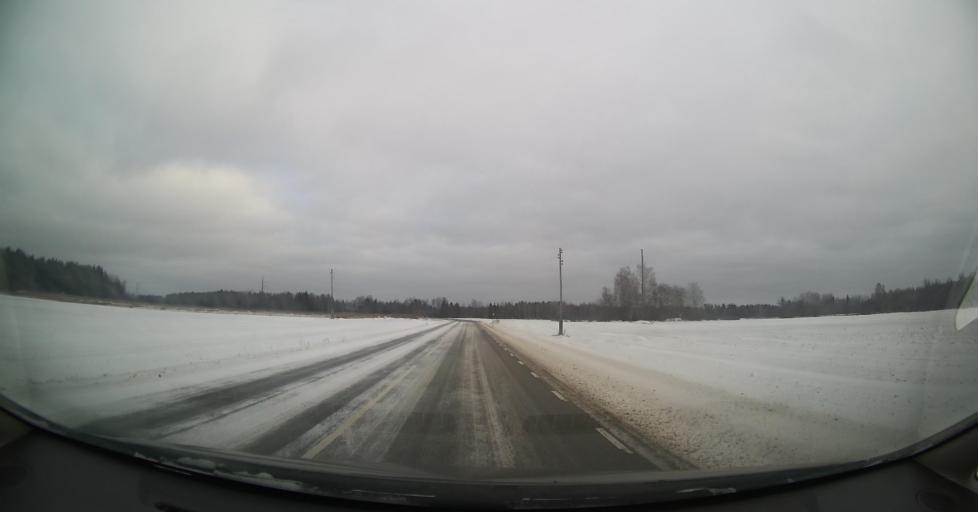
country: EE
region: Harju
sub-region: Anija vald
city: Kehra
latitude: 59.2616
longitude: 25.3415
